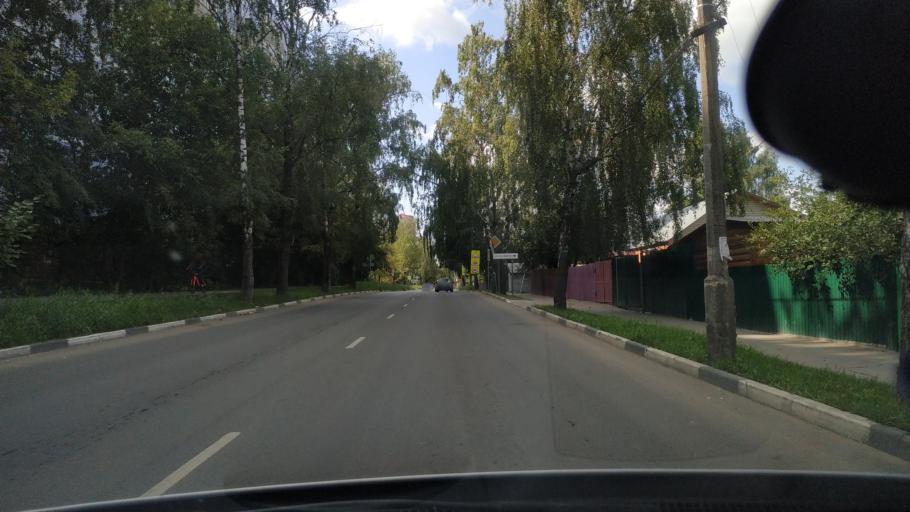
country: RU
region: Rjazan
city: Ryazan'
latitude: 54.6137
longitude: 39.7087
